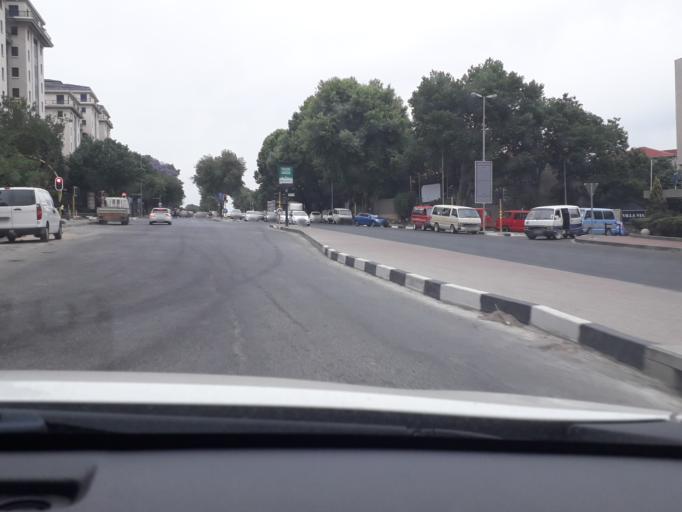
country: ZA
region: Gauteng
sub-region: City of Johannesburg Metropolitan Municipality
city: Johannesburg
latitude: -26.1038
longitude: 28.0603
